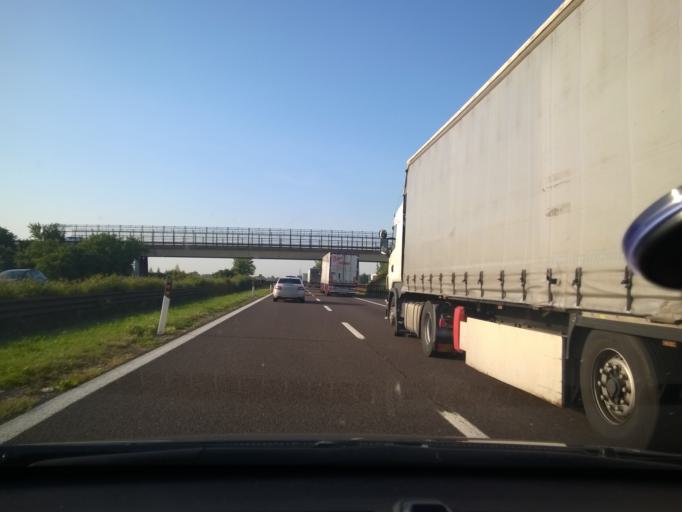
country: IT
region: Lombardy
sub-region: Provincia di Mantova
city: Stradella
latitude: 45.1475
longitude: 10.8669
